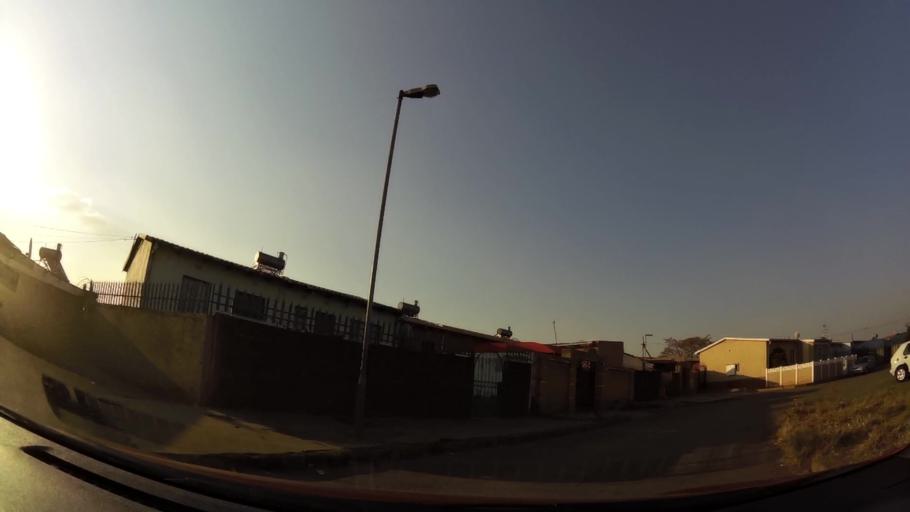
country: ZA
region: Gauteng
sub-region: City of Johannesburg Metropolitan Municipality
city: Soweto
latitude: -26.2867
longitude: 27.8939
